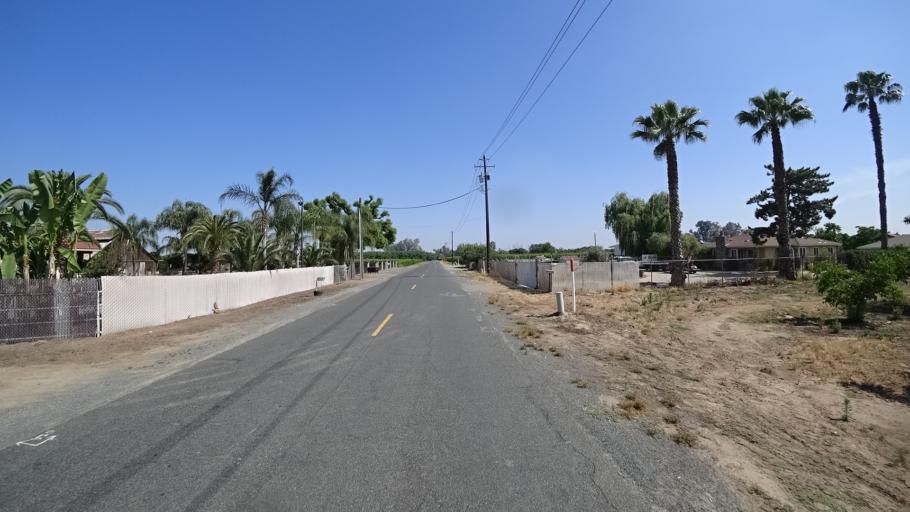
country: US
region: California
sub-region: Fresno County
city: Kingsburg
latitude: 36.4786
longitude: -119.5507
